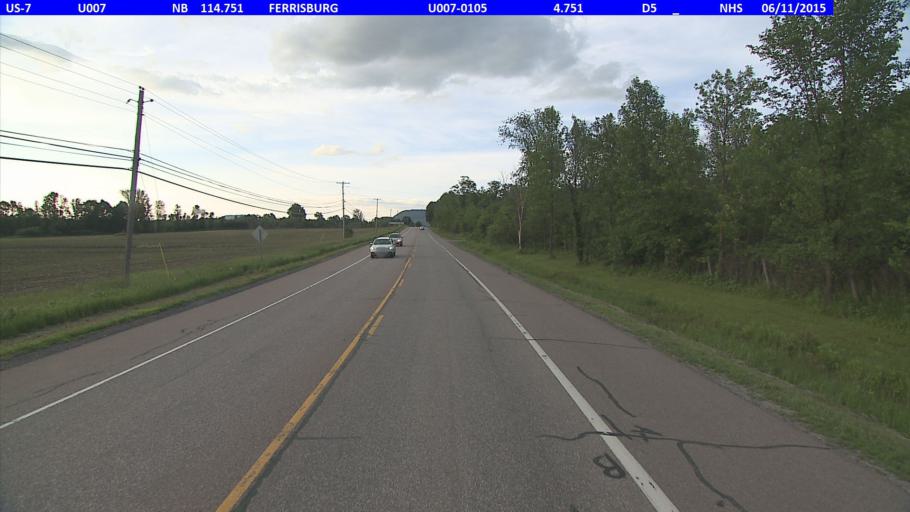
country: US
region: Vermont
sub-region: Addison County
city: Vergennes
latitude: 44.2278
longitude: -73.2355
